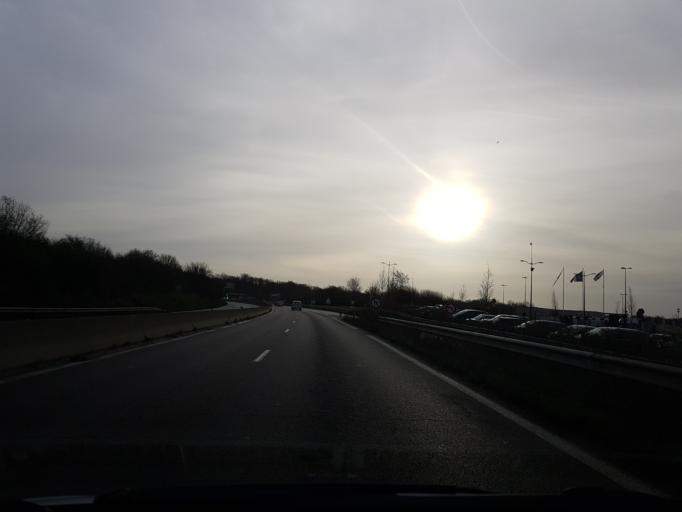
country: FR
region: Ile-de-France
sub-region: Departement de l'Essonne
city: Montgeron
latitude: 48.6928
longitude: 2.4493
